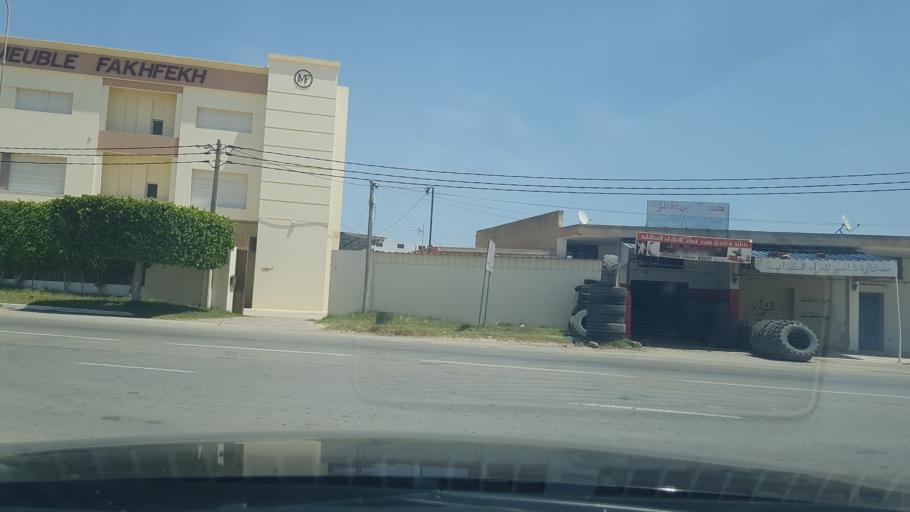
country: TN
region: Safaqis
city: Al Qarmadah
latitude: 34.8446
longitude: 10.7625
